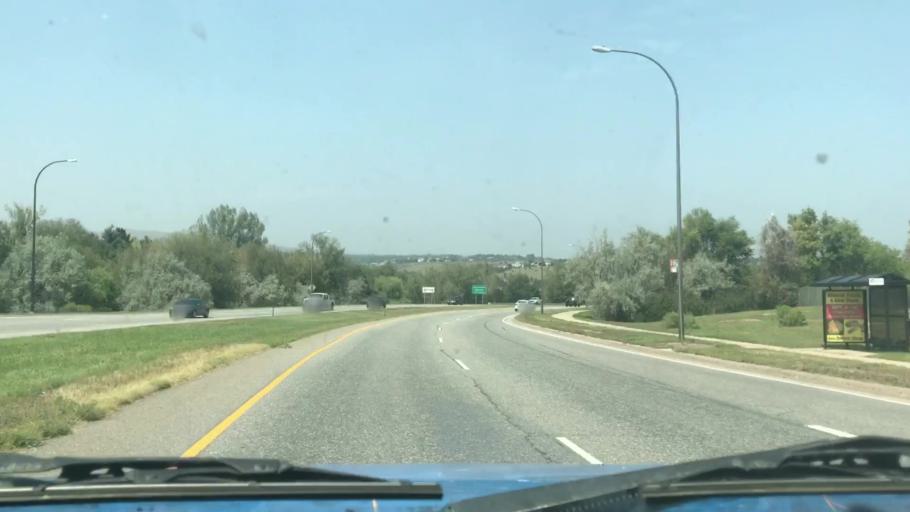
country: US
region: Colorado
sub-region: Jefferson County
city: Lakewood
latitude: 39.6566
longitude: -105.1112
